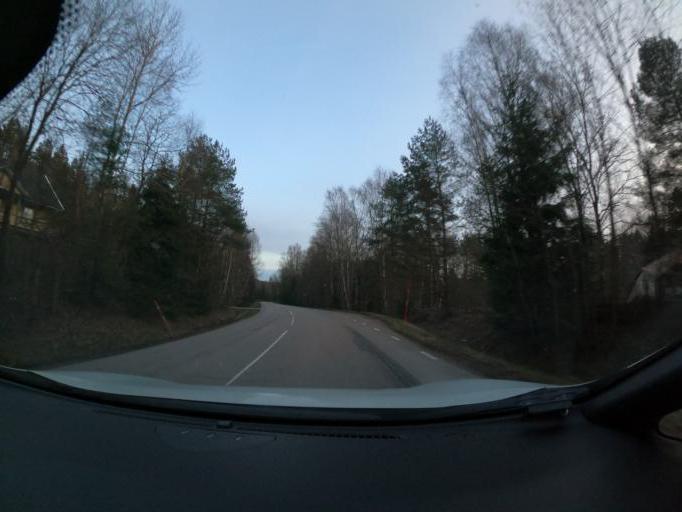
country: SE
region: Vaestra Goetaland
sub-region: Harryda Kommun
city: Landvetter
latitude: 57.6321
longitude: 12.1780
